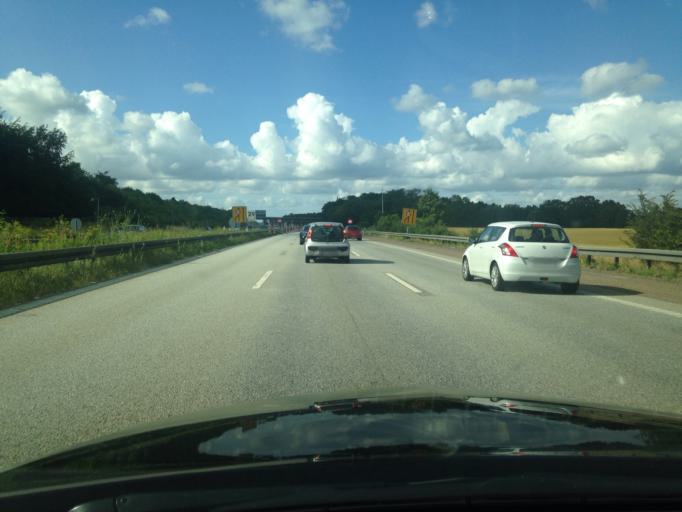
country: DK
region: Capital Region
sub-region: Rudersdal Kommune
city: Trorod
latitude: 55.8227
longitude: 12.5262
